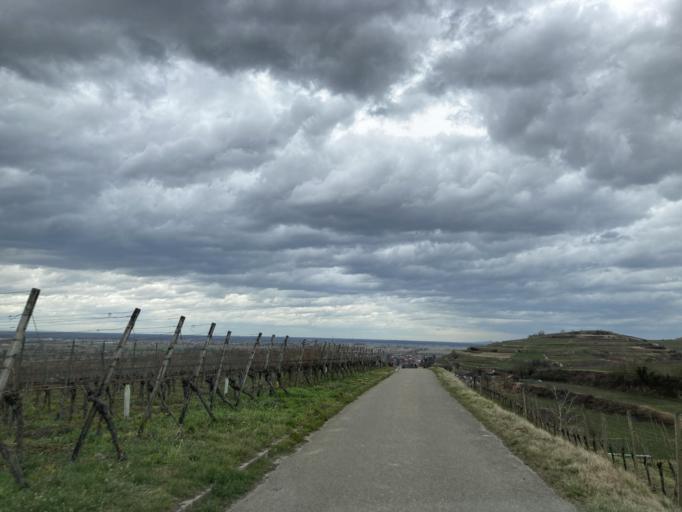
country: DE
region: Baden-Wuerttemberg
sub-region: Freiburg Region
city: Vogtsburg
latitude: 48.1205
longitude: 7.6485
